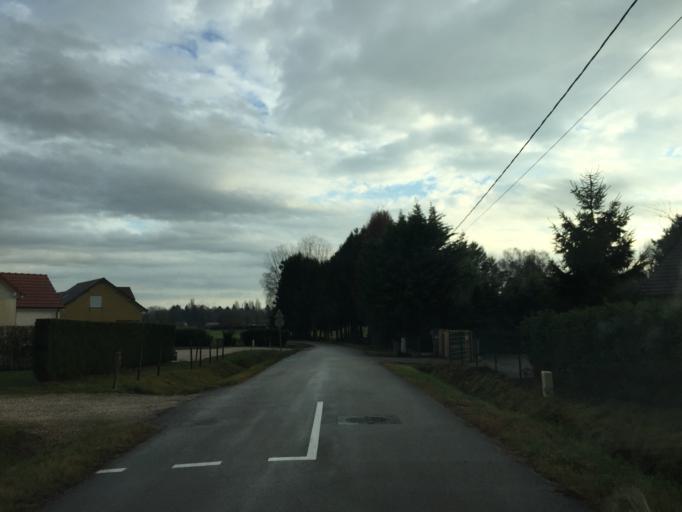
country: FR
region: Franche-Comte
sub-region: Departement du Jura
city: Mont-sous-Vaudrey
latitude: 46.9797
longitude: 5.5894
